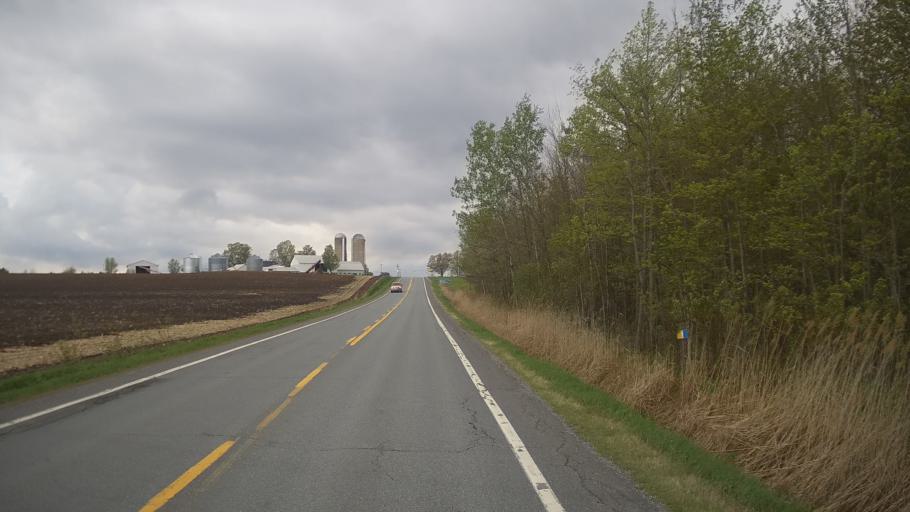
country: CA
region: Quebec
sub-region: Monteregie
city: Farnham
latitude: 45.2650
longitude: -72.9365
